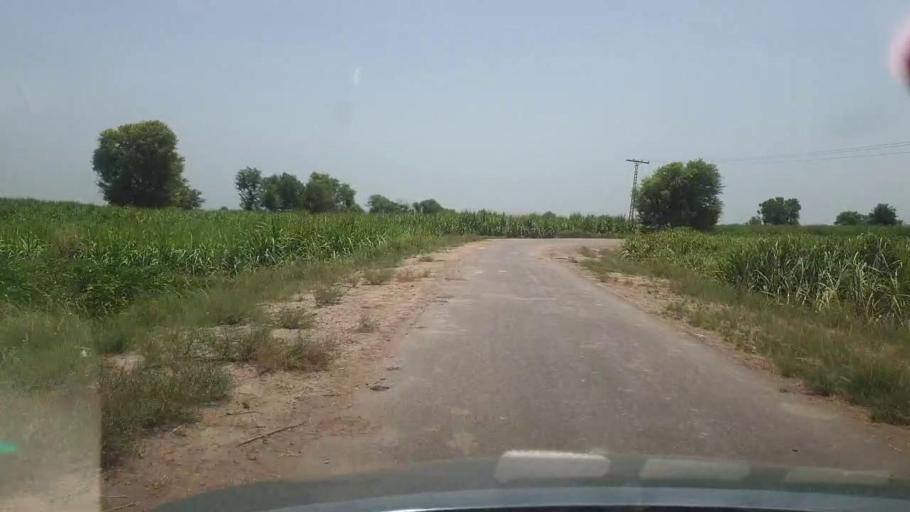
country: PK
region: Sindh
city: Hingorja
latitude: 27.2268
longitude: 68.3204
